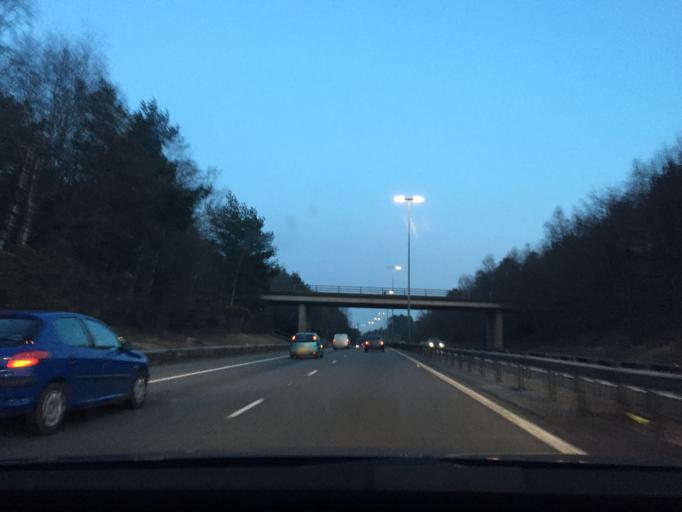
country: GB
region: England
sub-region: Southampton
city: Southampton
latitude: 50.9558
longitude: -1.4118
